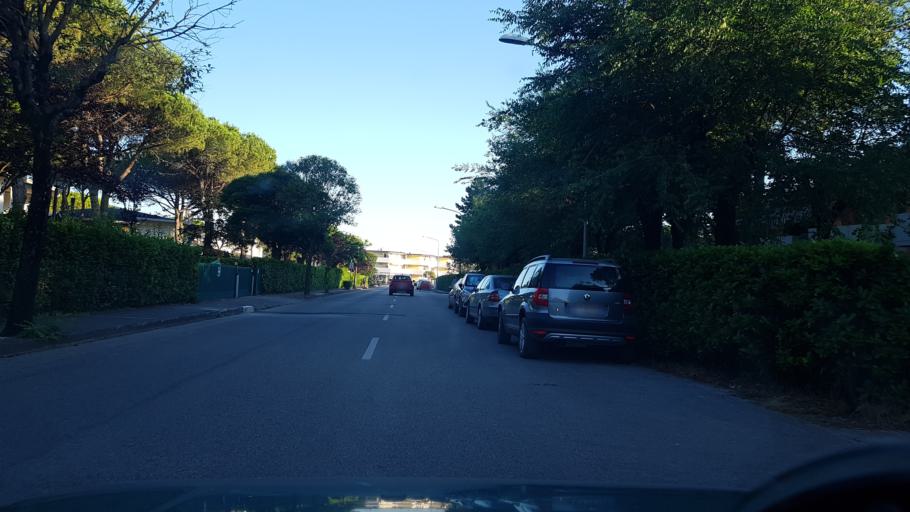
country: IT
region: Veneto
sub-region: Provincia di Venezia
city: Bibione
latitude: 45.6438
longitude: 13.0435
